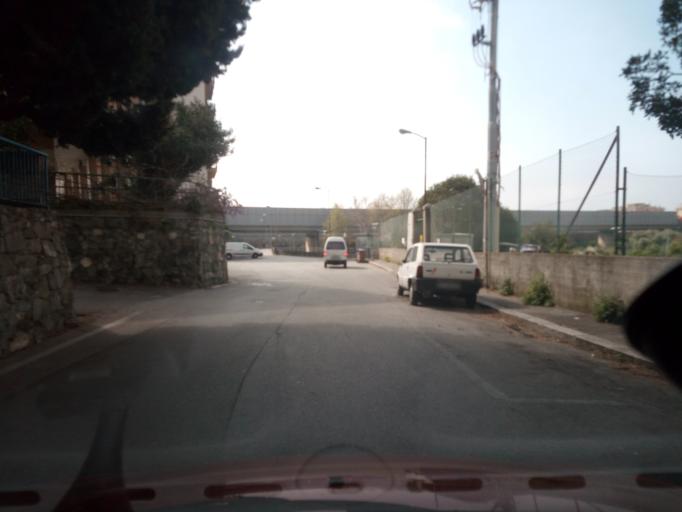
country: IT
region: Liguria
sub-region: Provincia di Genova
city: Mele
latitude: 44.4316
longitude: 8.7781
